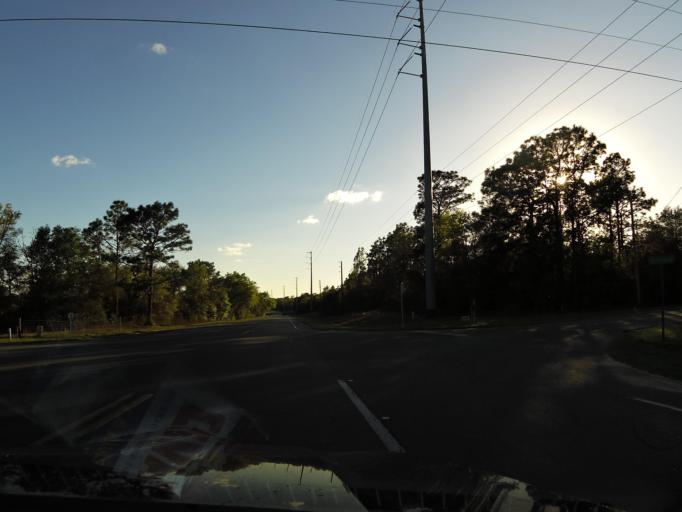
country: US
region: Florida
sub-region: Clay County
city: Keystone Heights
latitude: 29.8073
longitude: -82.0115
